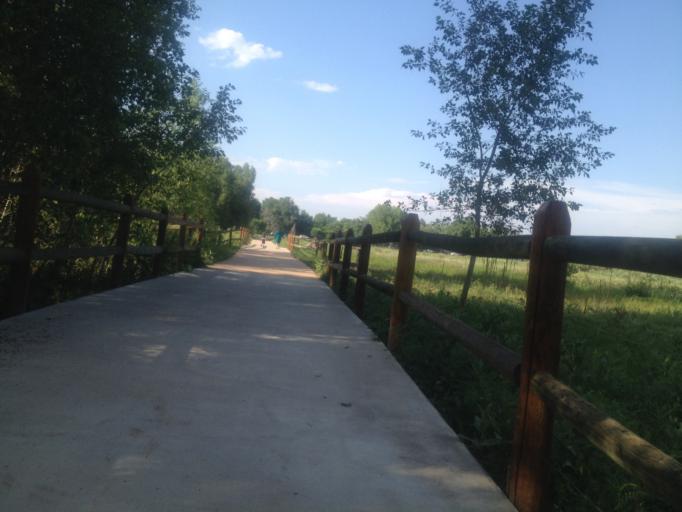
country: US
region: Colorado
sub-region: Boulder County
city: Boulder
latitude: 39.9972
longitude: -105.2150
